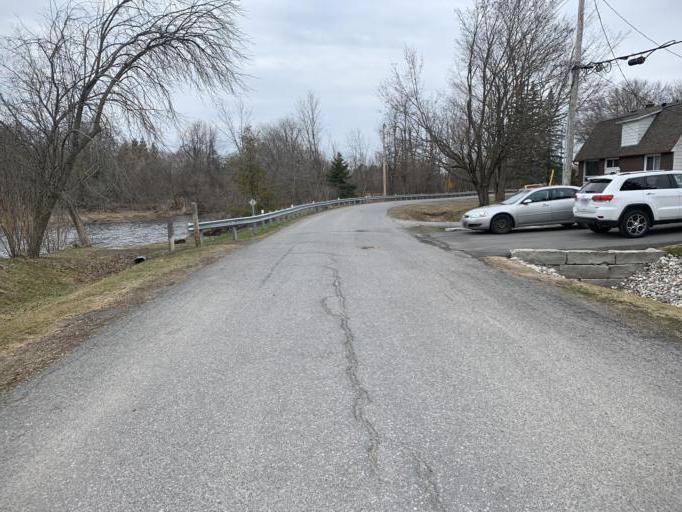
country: CA
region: Ontario
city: Bells Corners
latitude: 45.1848
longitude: -75.8321
